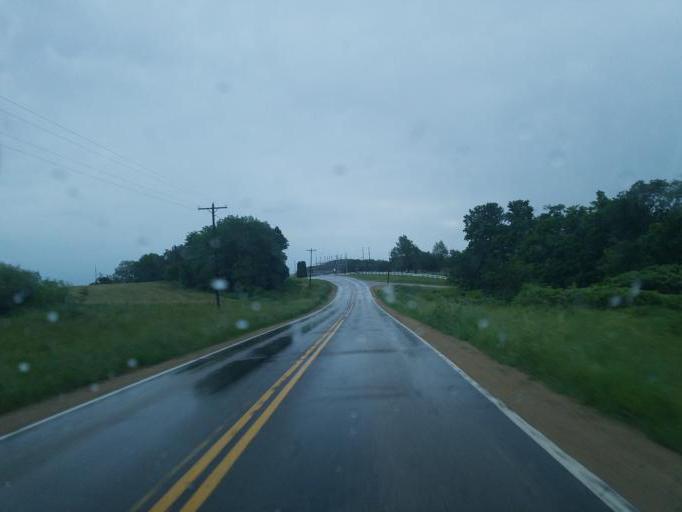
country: US
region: Wisconsin
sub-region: Vernon County
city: Hillsboro
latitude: 43.6685
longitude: -90.4637
